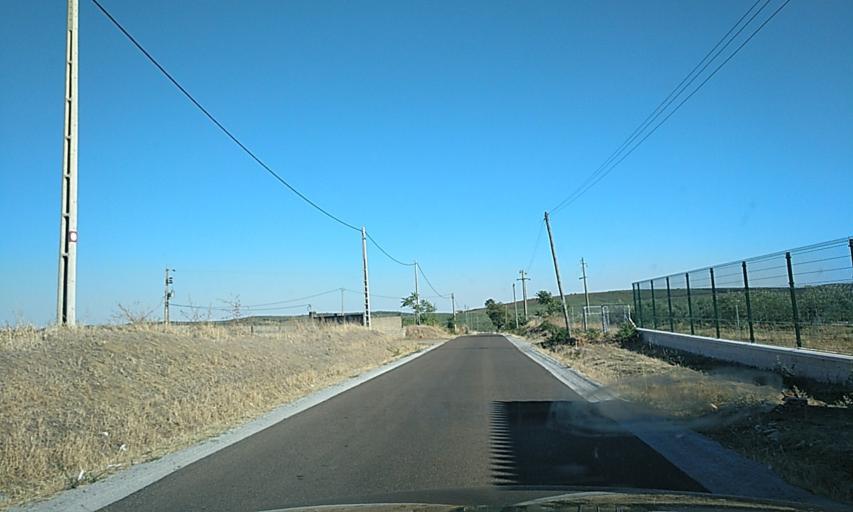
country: PT
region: Portalegre
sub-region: Campo Maior
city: Campo Maior
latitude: 39.0096
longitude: -7.0631
